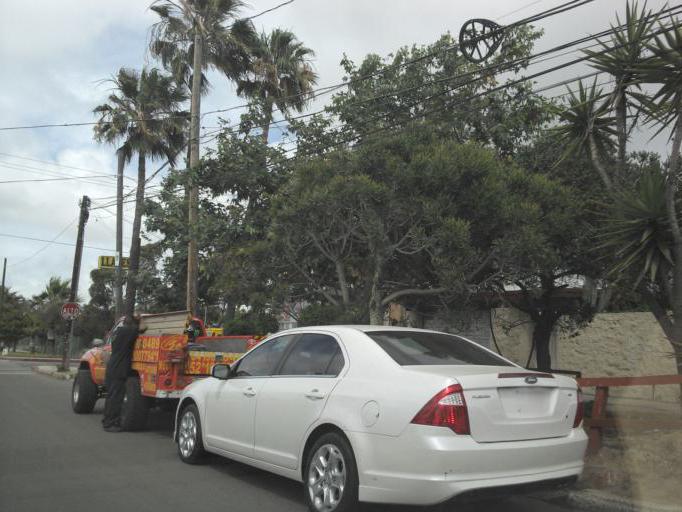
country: MX
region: Baja California
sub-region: Tijuana
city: La Esperanza [Granjas Familiares]
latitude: 32.5196
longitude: -117.1161
